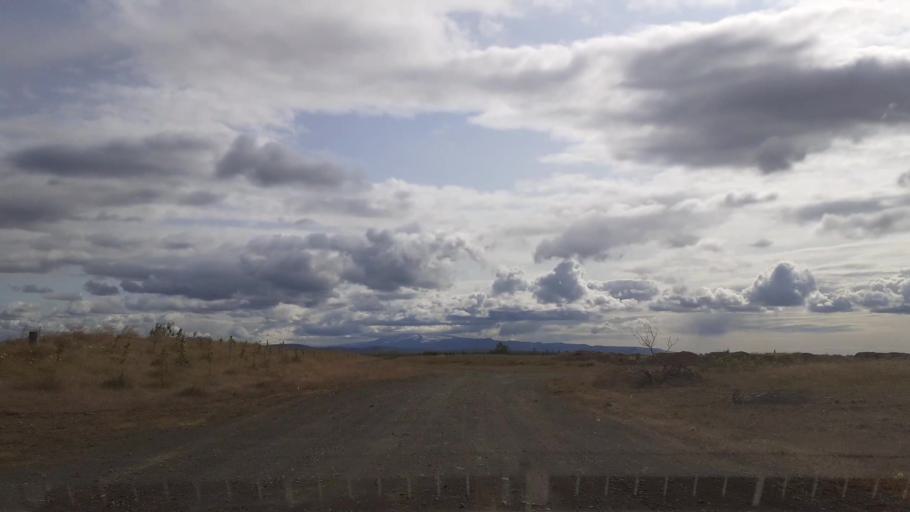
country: IS
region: South
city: Vestmannaeyjar
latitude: 63.8287
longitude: -20.4019
